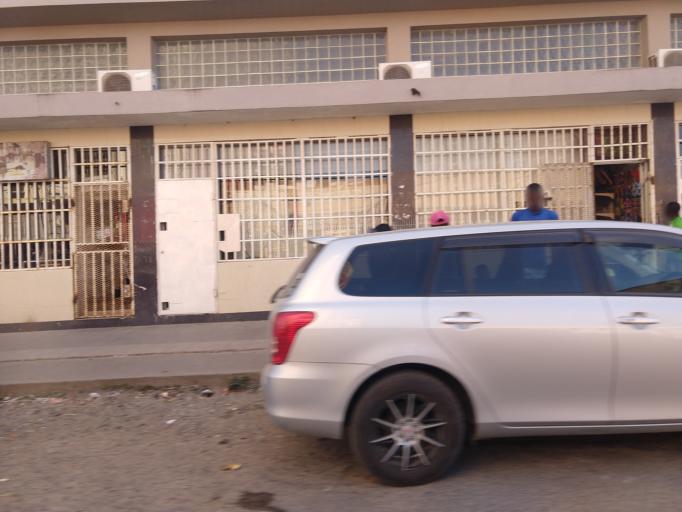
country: MZ
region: Sofala
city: Beira
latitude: -19.8306
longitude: 34.8426
